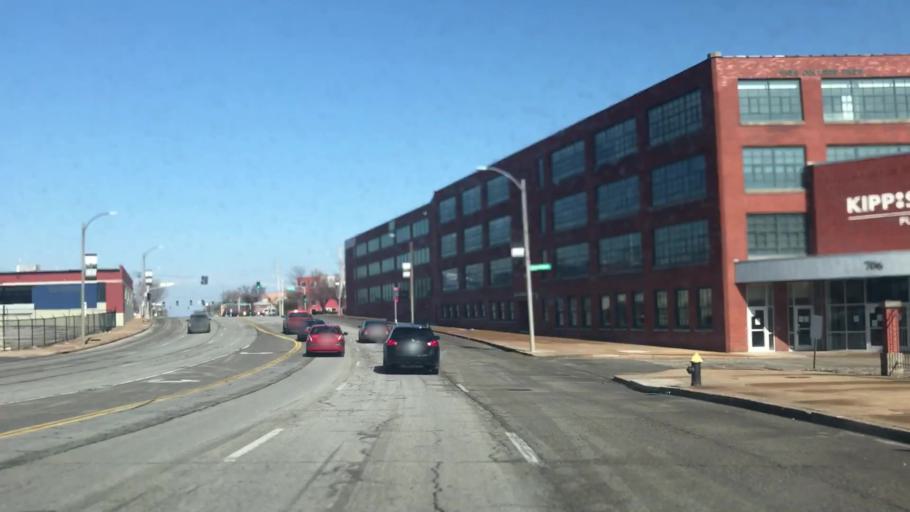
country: US
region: Missouri
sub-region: City of Saint Louis
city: St. Louis
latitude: 38.6355
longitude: -90.2129
